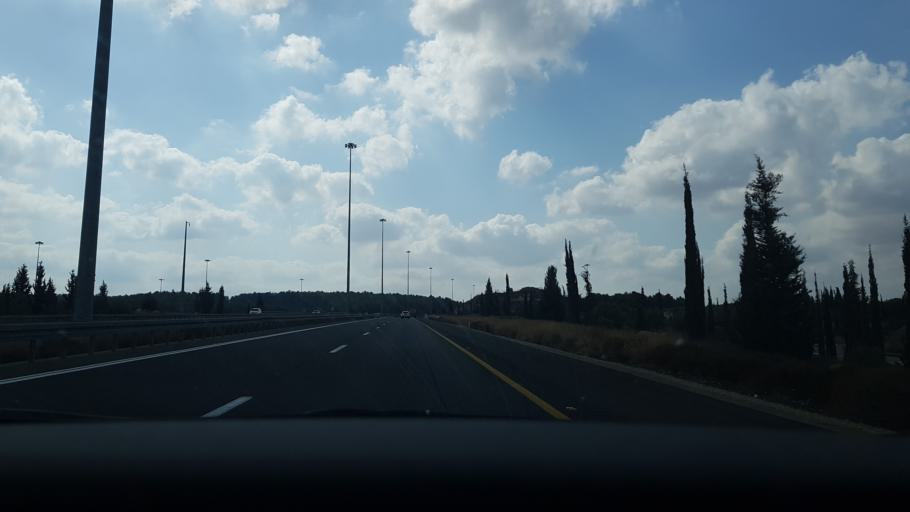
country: IL
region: Southern District
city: Qiryat Gat
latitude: 31.6019
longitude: 34.8131
